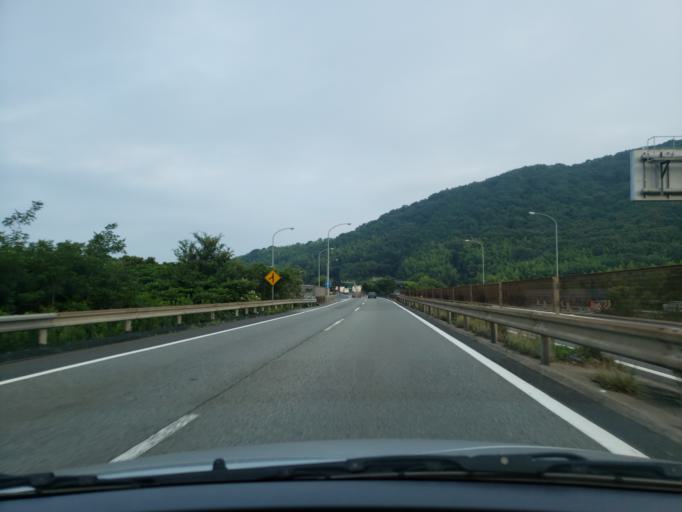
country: JP
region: Hyogo
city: Tatsunocho-tominaga
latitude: 34.8467
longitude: 134.6018
